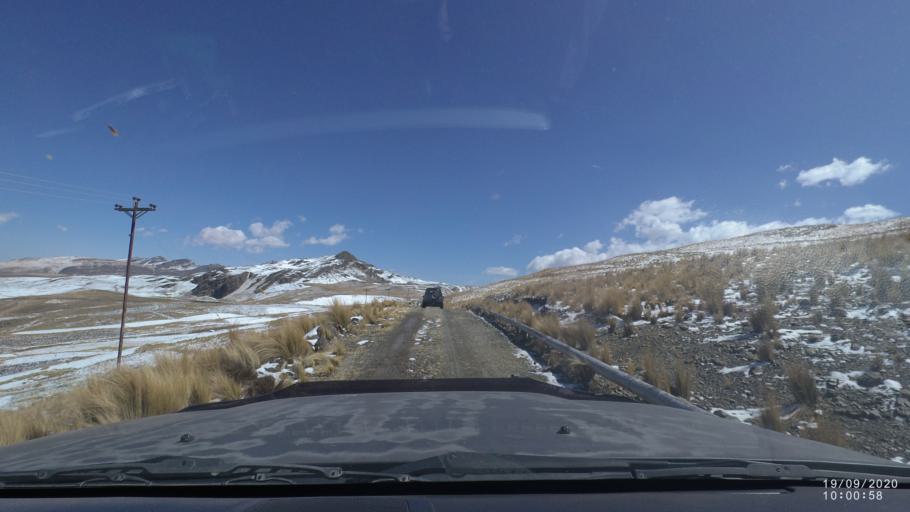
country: BO
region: Cochabamba
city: Cochabamba
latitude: -17.3031
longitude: -66.0903
